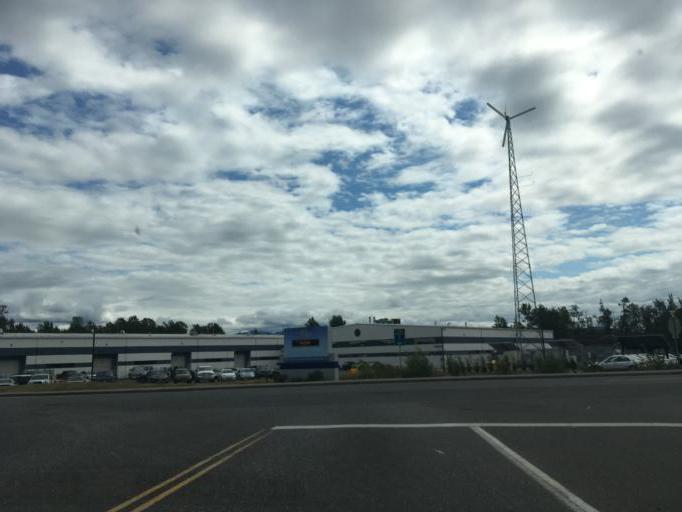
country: US
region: Washington
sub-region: Whatcom County
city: Marietta-Alderwood
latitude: 48.7857
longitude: -122.5262
